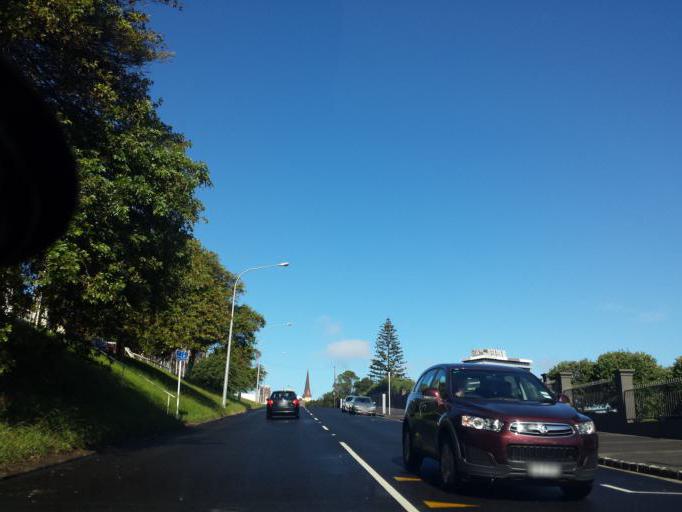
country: NZ
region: Auckland
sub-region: Auckland
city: Auckland
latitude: -36.8616
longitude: 174.7658
